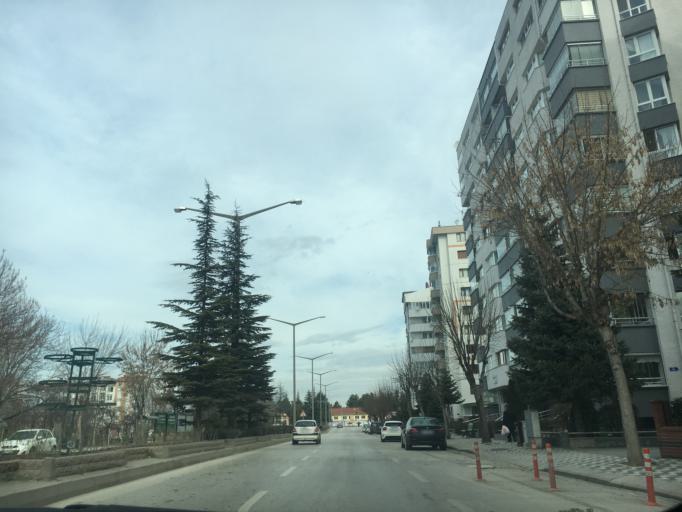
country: TR
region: Eskisehir
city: Eskisehir
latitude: 39.7719
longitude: 30.5013
